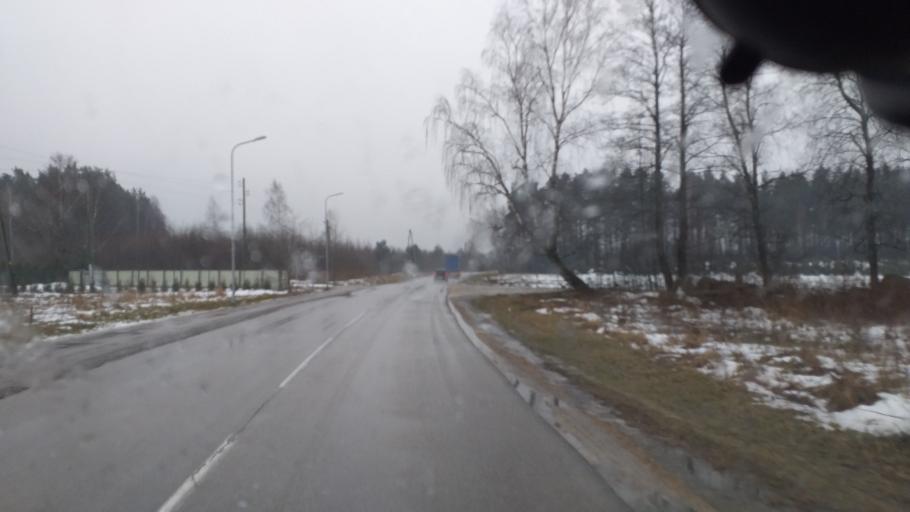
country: LV
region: Babite
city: Pinki
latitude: 56.9729
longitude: 23.9693
